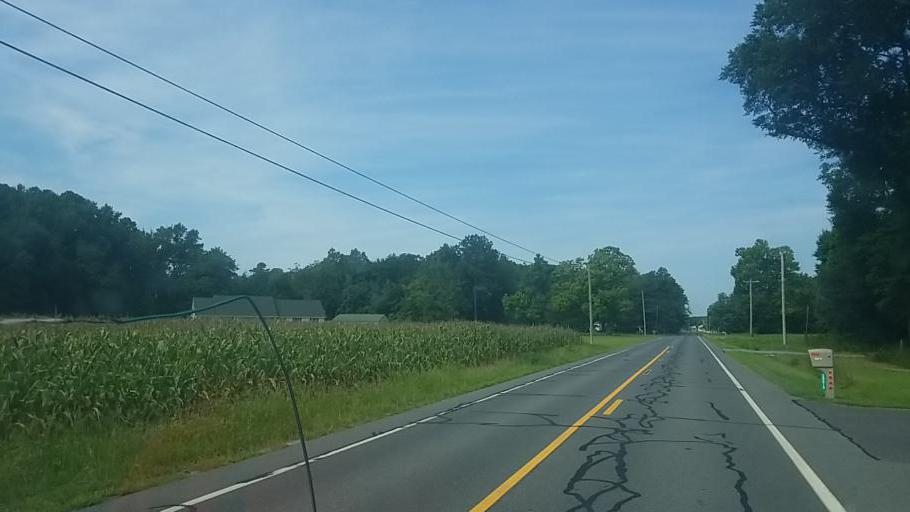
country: US
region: Delaware
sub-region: Sussex County
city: Selbyville
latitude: 38.5267
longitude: -75.2110
